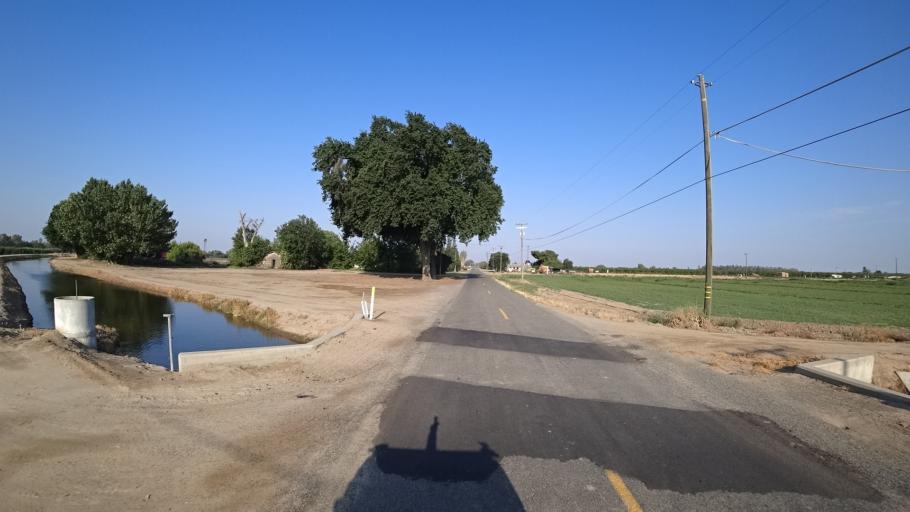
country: US
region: California
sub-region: Kings County
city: Lemoore
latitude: 36.3730
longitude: -119.8013
